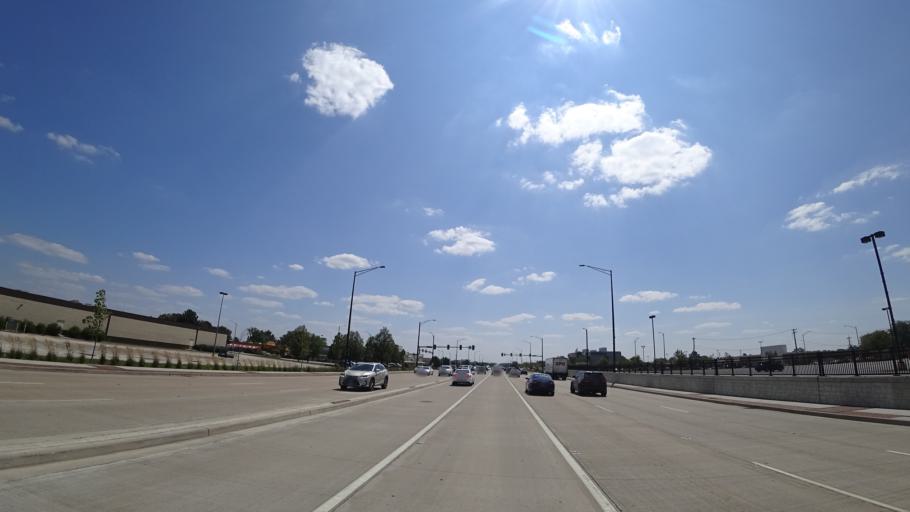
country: US
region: Illinois
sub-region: Cook County
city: Orland Park
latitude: 41.6171
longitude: -87.8535
